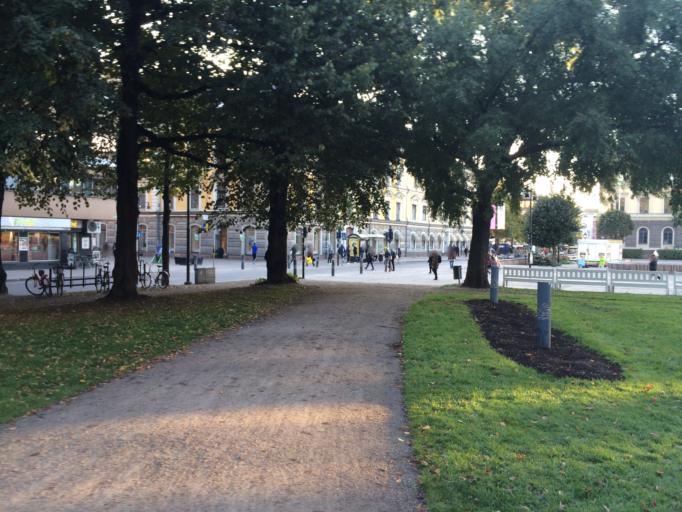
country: SE
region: Gaevleborg
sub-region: Gavle Kommun
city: Gavle
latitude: 60.6751
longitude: 17.1442
